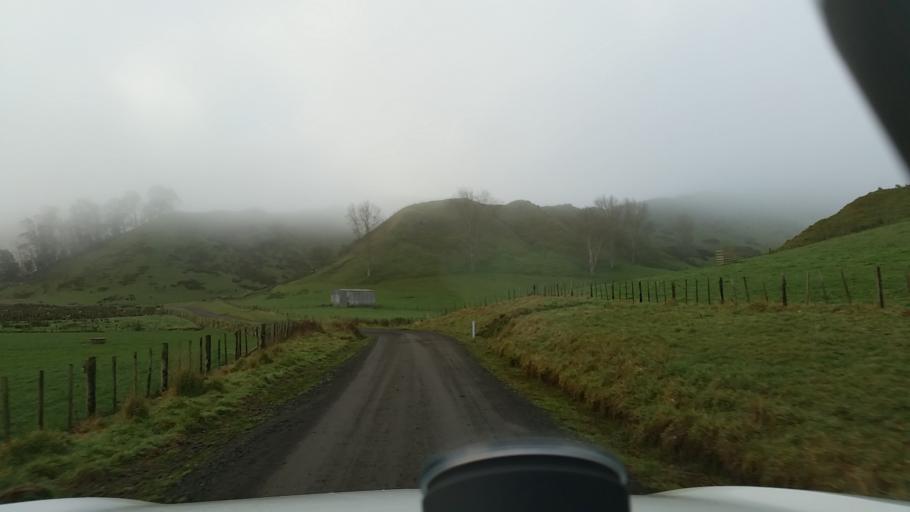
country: NZ
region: Taranaki
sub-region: South Taranaki District
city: Eltham
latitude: -39.4297
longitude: 174.4401
